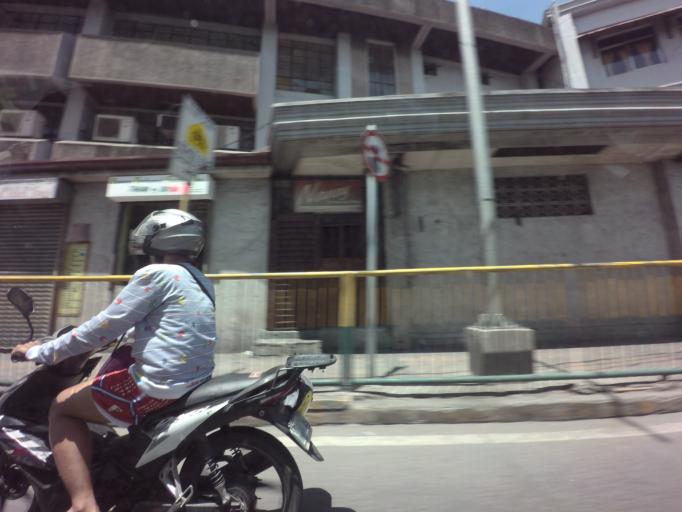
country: PH
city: Sambayanihan People's Village
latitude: 14.5002
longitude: 120.9915
